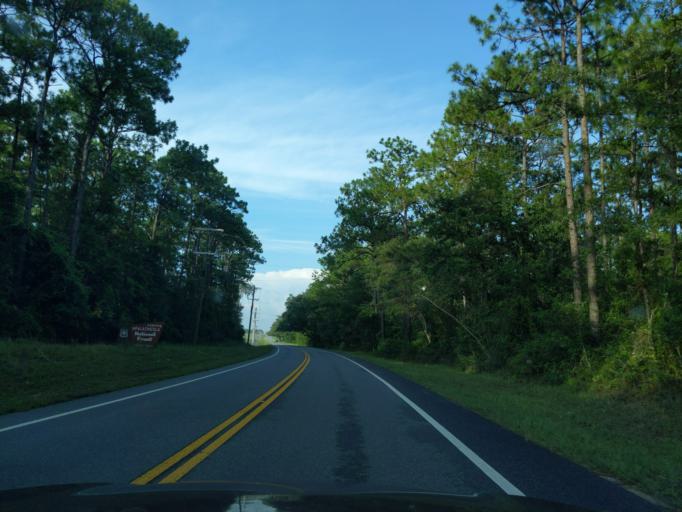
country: US
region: Florida
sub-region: Leon County
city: Tallahassee
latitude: 30.3863
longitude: -84.3321
